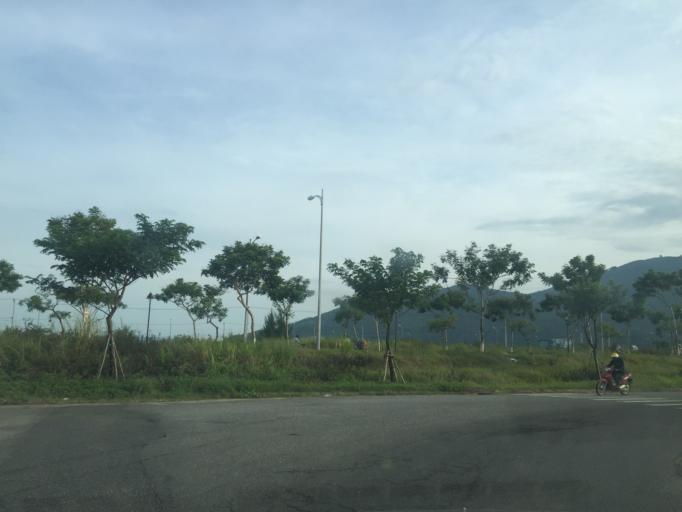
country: VN
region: Da Nang
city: Da Nang
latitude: 16.0996
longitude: 108.2302
